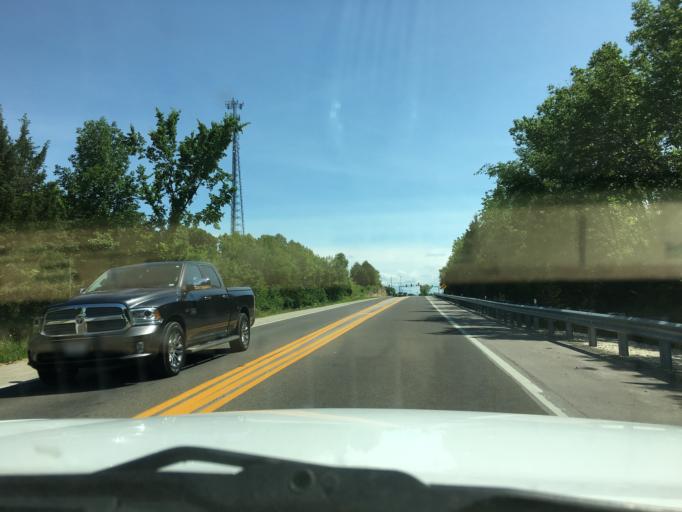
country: US
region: Missouri
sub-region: Franklin County
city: Union
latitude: 38.4850
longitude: -91.0052
